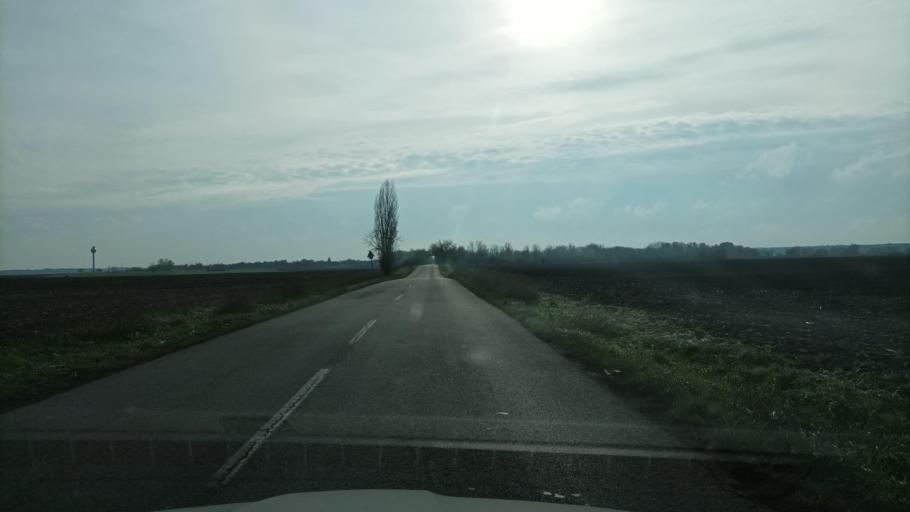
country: HU
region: Pest
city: Rackeve
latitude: 47.1041
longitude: 18.9265
